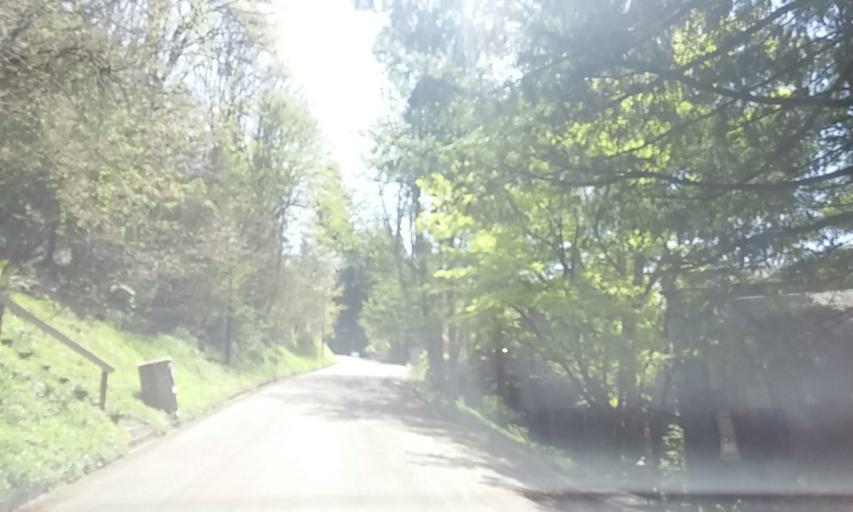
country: US
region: Oregon
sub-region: Washington County
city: West Haven-Sylvan
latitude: 45.5176
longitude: -122.7635
